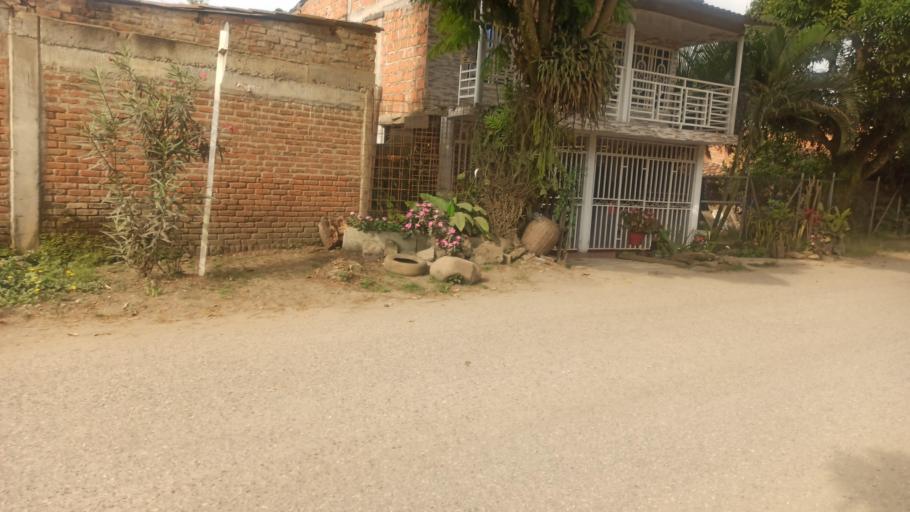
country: CO
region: Valle del Cauca
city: Jamundi
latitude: 3.2005
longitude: -76.5032
